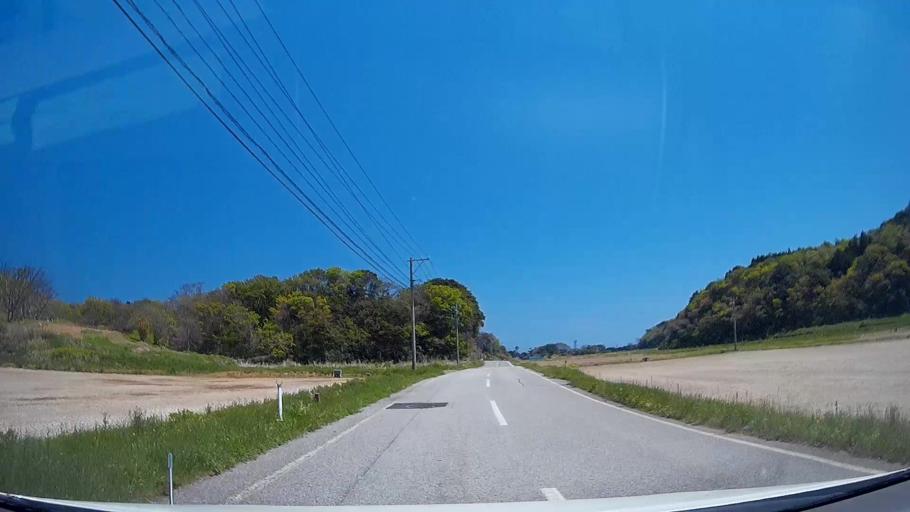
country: JP
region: Ishikawa
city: Nanao
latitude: 37.5253
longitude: 137.3156
